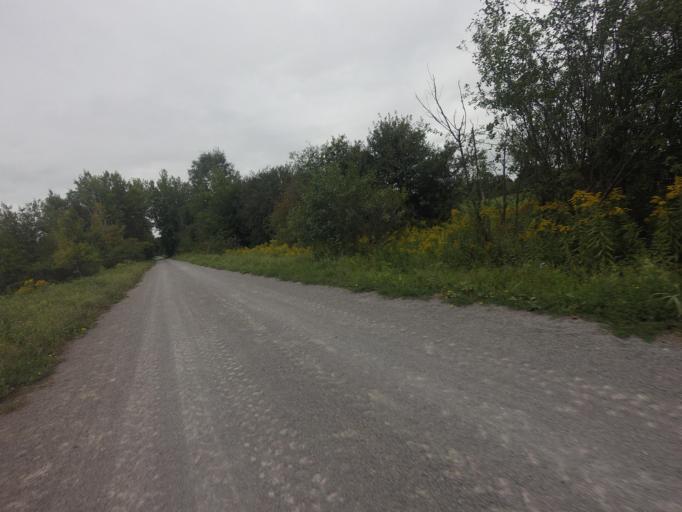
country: CA
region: Ontario
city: Omemee
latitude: 44.4012
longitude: -78.7599
